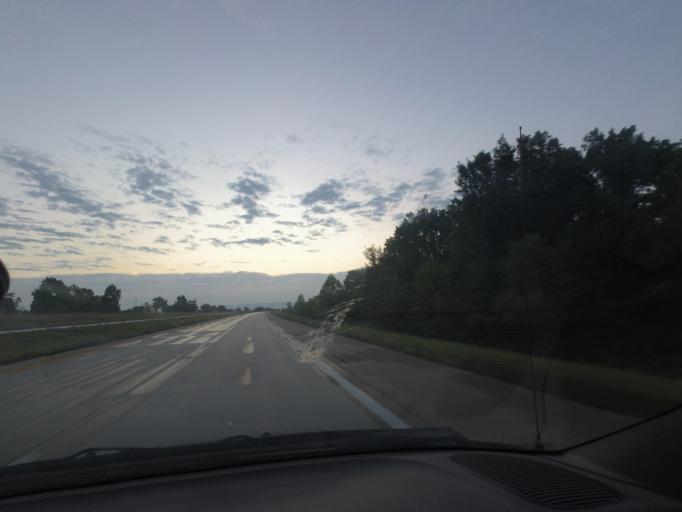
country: US
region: Missouri
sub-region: Macon County
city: Macon
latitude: 39.7603
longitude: -92.5850
